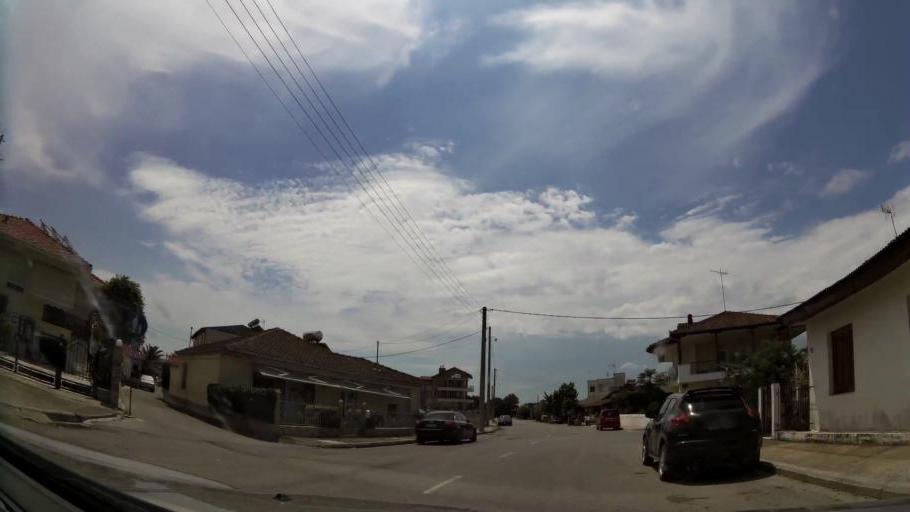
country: GR
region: Central Macedonia
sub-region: Nomos Pierias
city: Katerini
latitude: 40.2610
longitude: 22.5000
